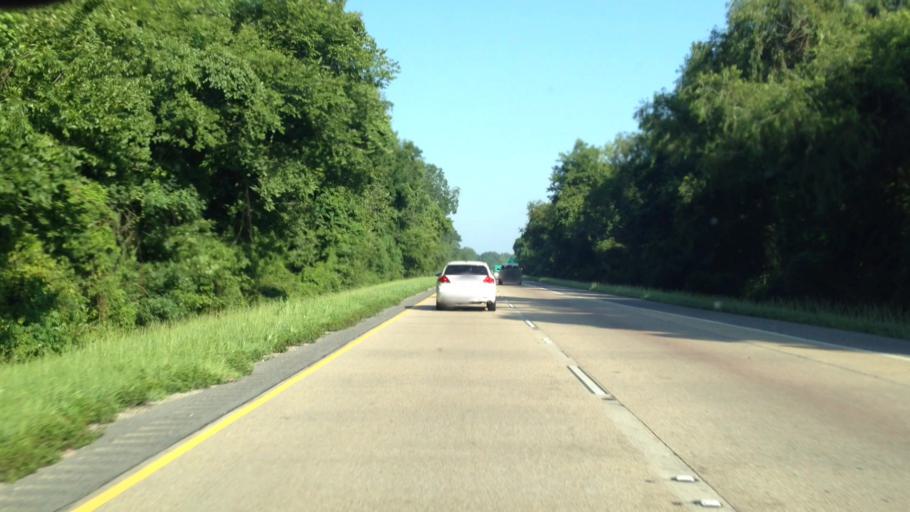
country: US
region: Louisiana
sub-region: Ascension Parish
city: Gonzales
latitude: 30.1961
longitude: -90.9271
